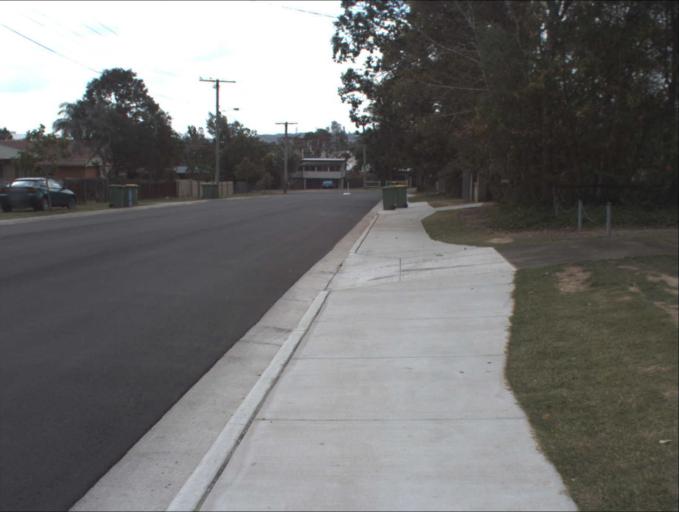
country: AU
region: Queensland
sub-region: Logan
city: Waterford West
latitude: -27.6732
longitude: 153.1423
